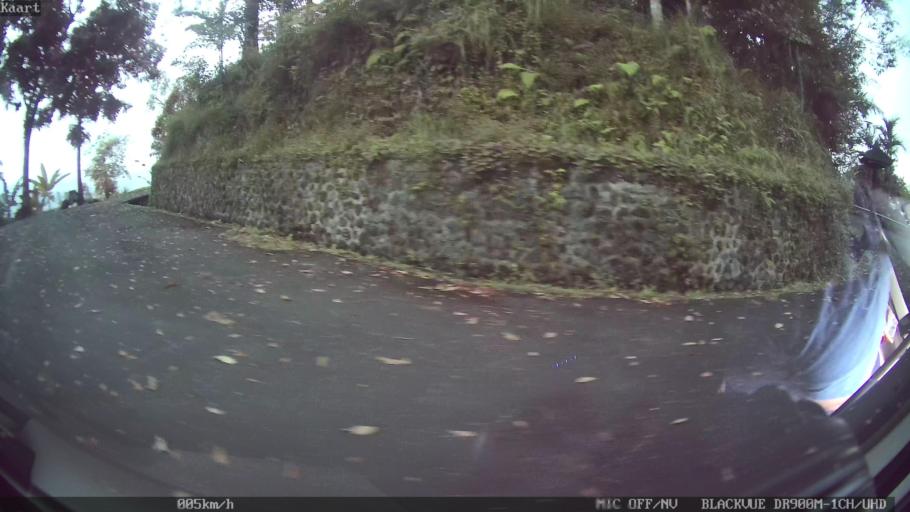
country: ID
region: Bali
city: Peneng
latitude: -8.3671
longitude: 115.2129
